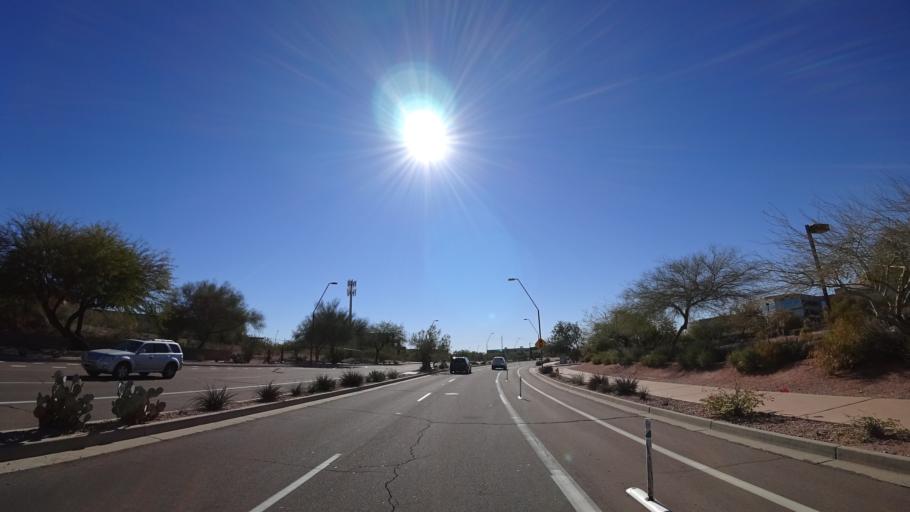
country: US
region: Arizona
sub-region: Maricopa County
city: Tempe Junction
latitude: 33.4467
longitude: -111.9552
